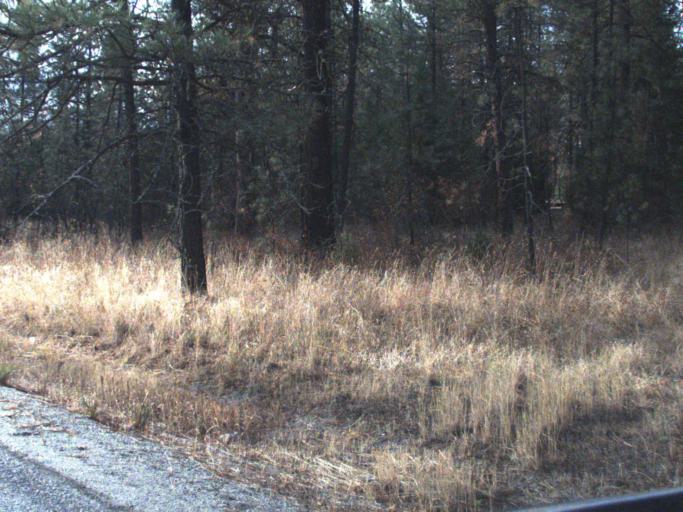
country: US
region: Washington
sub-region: Stevens County
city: Kettle Falls
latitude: 48.8051
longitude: -118.1626
